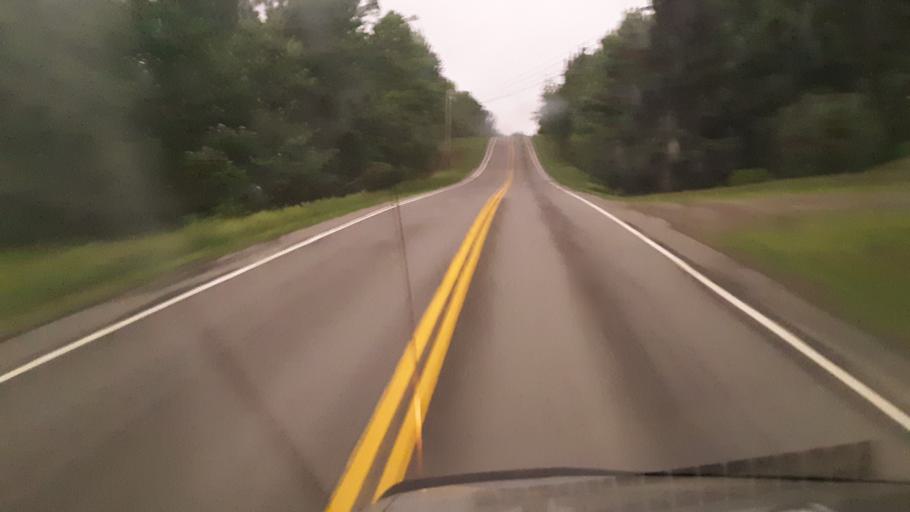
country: US
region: Maine
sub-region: Penobscot County
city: Patten
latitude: 46.0853
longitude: -68.4291
